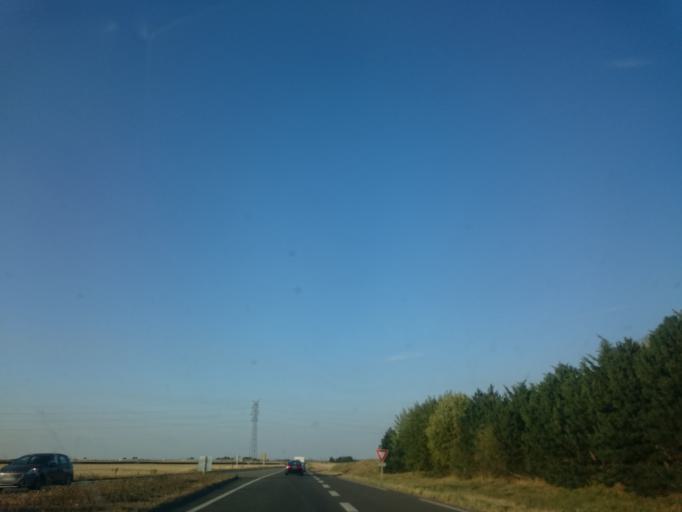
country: FR
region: Centre
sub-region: Departement d'Eure-et-Loir
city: Toury
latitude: 48.2018
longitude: 1.9361
